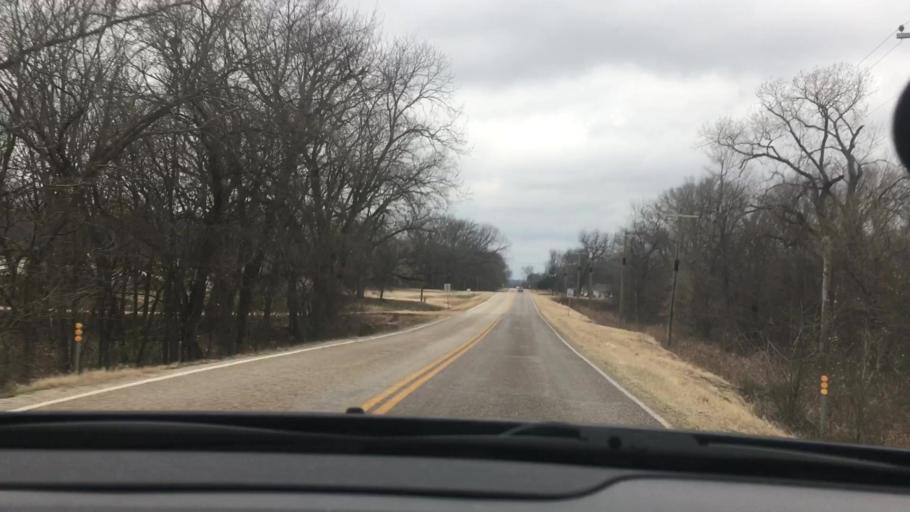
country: US
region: Oklahoma
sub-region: Coal County
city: Coalgate
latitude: 34.3750
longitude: -96.4273
